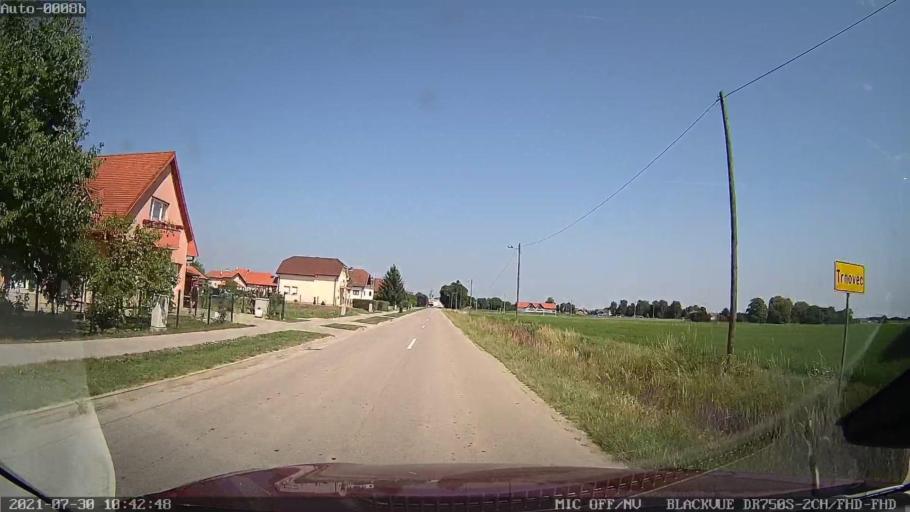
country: HR
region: Medimurska
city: Kursanec
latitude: 46.2882
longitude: 16.4076
